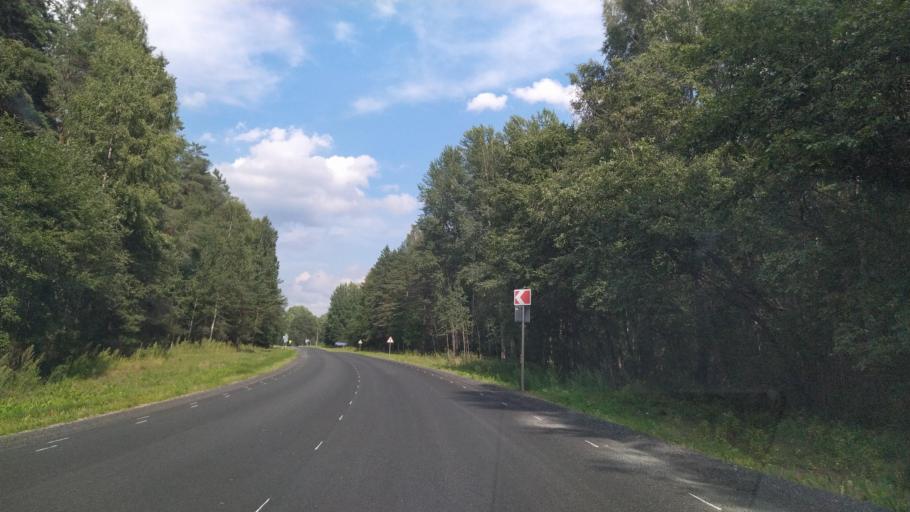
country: RU
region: Pskov
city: Porkhov
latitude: 57.7357
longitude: 29.4131
